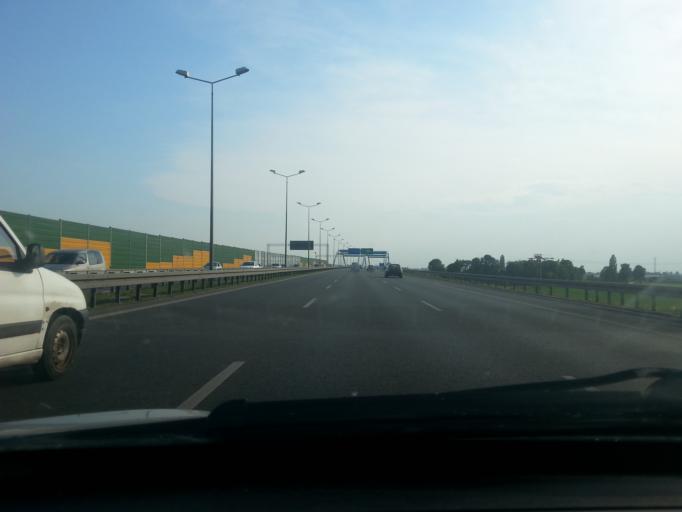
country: PL
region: Masovian Voivodeship
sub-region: Powiat pruszkowski
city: Piastow
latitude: 52.2101
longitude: 20.8563
